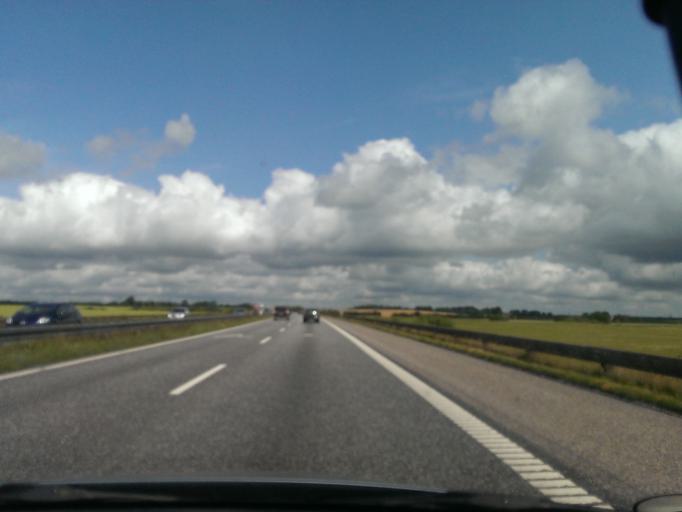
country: DK
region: North Denmark
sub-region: Mariagerfjord Kommune
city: Hobro
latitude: 56.7174
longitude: 9.7236
